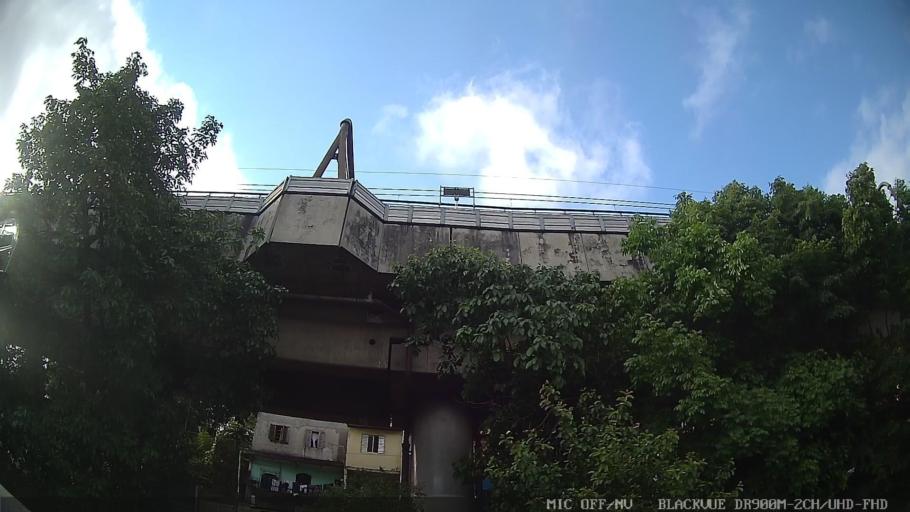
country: BR
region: Sao Paulo
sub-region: Taboao Da Serra
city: Taboao da Serra
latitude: -23.6461
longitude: -46.7561
